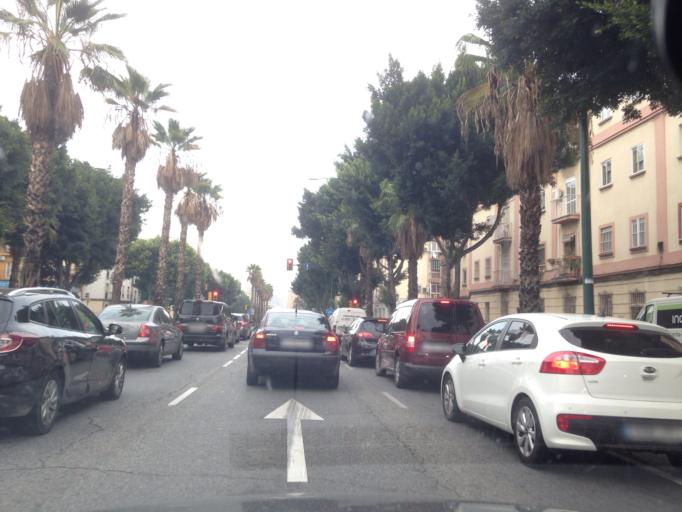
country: ES
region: Andalusia
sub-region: Provincia de Malaga
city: Malaga
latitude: 36.7158
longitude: -4.4439
